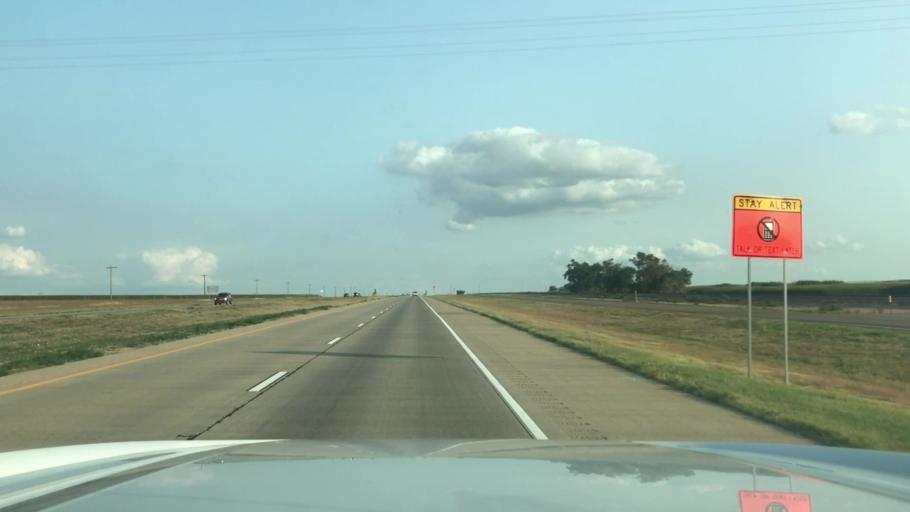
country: US
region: Texas
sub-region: Swisher County
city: Tulia
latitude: 34.6031
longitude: -101.8064
